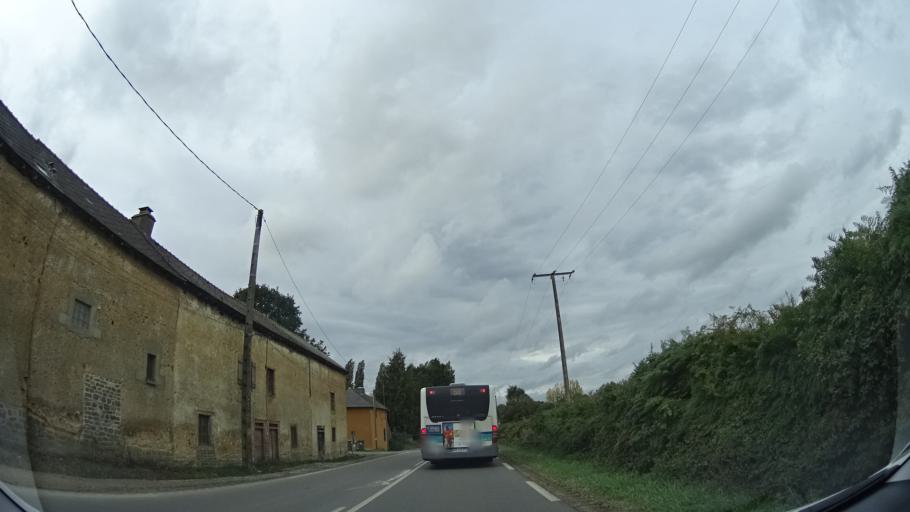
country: FR
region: Brittany
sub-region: Departement d'Ille-et-Vilaine
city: La Meziere
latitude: 48.2122
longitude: -1.7662
